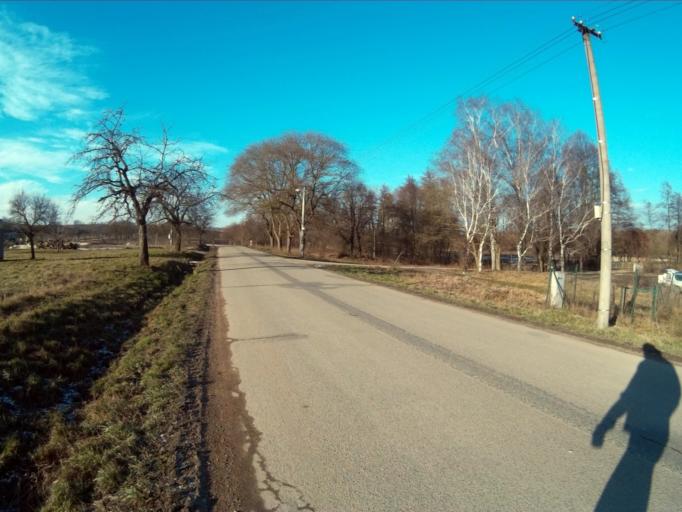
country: CZ
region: South Moravian
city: Krenovice
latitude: 49.1506
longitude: 16.8255
